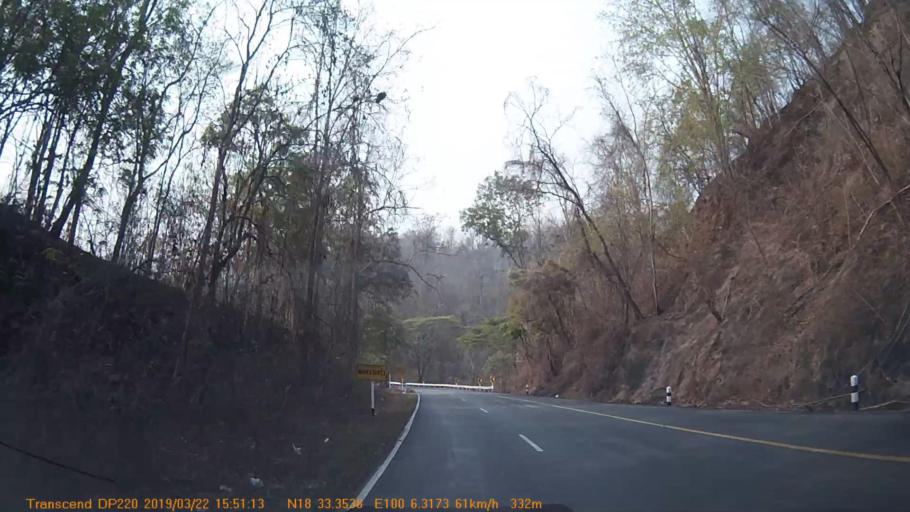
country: TH
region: Phrae
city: Song
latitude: 18.5562
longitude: 100.1053
